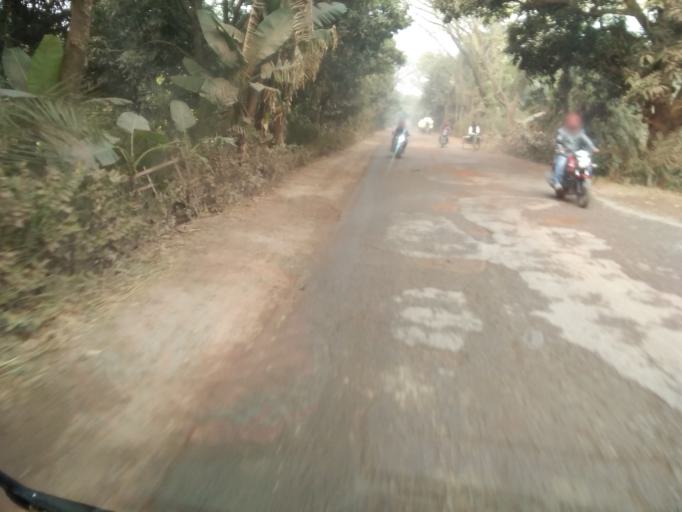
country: BD
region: Khulna
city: Satkhira
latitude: 22.6841
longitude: 89.0280
